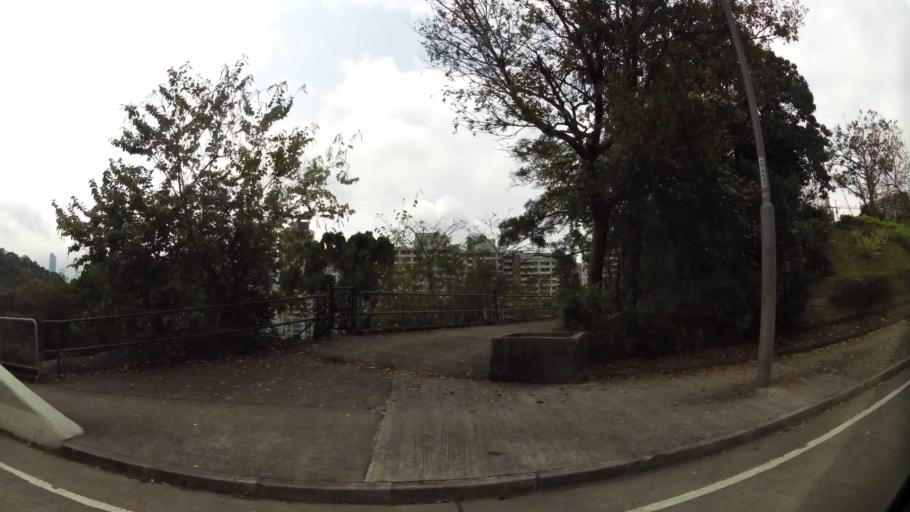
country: HK
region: Sham Shui Po
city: Sham Shui Po
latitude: 22.3406
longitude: 114.1613
